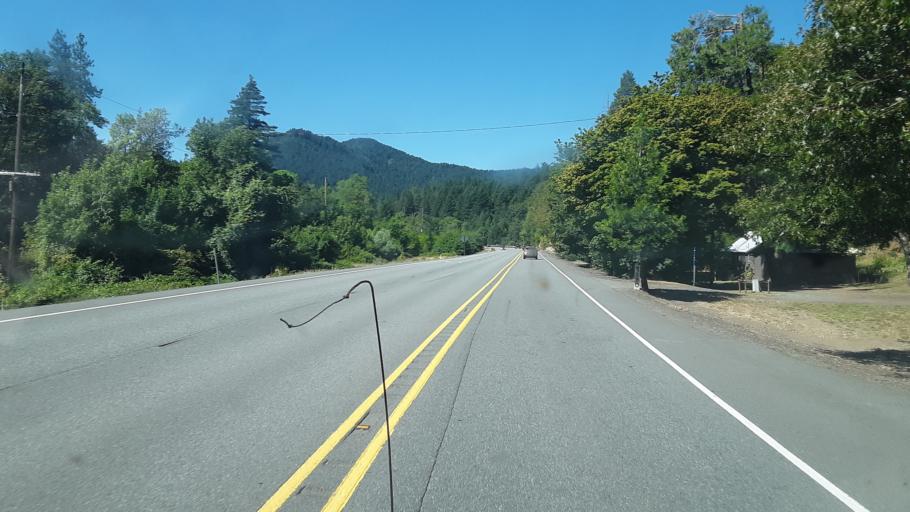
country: US
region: Oregon
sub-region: Josephine County
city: Redwood
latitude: 42.3718
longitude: -123.5019
